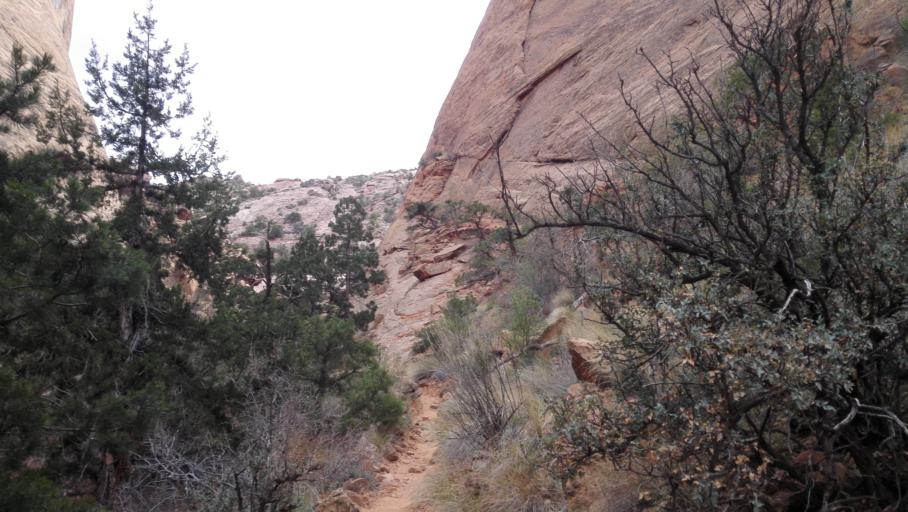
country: US
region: Utah
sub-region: Grand County
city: Moab
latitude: 38.4519
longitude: -109.9289
